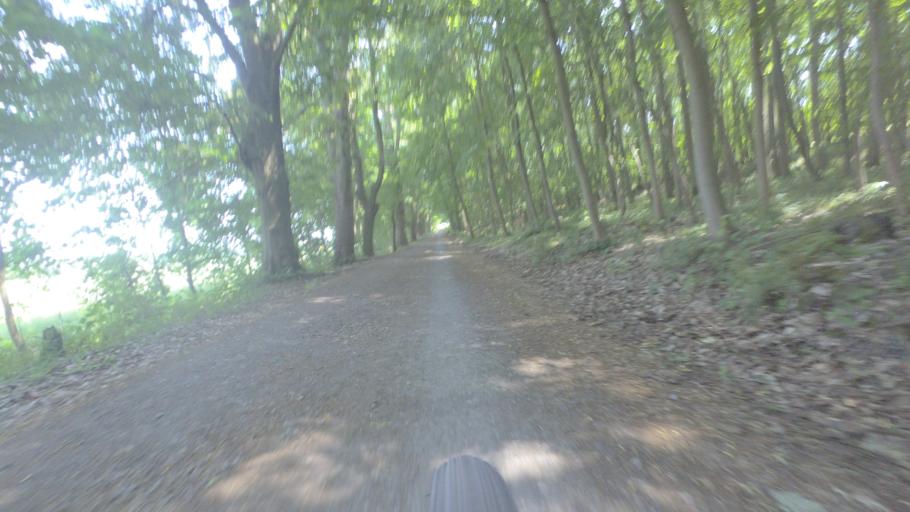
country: DE
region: Saxony-Anhalt
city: Ballenstedt
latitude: 51.7224
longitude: 11.2046
